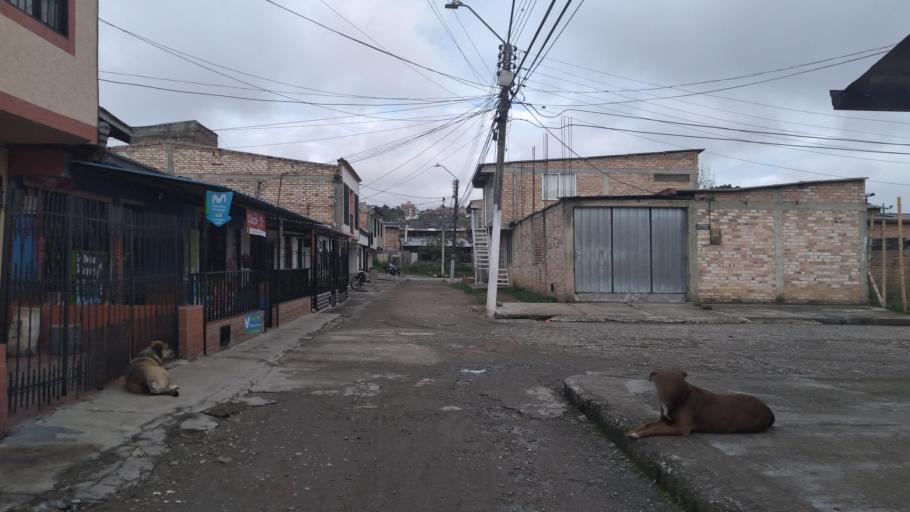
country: CO
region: Cauca
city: Popayan
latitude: 2.4294
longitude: -76.6106
